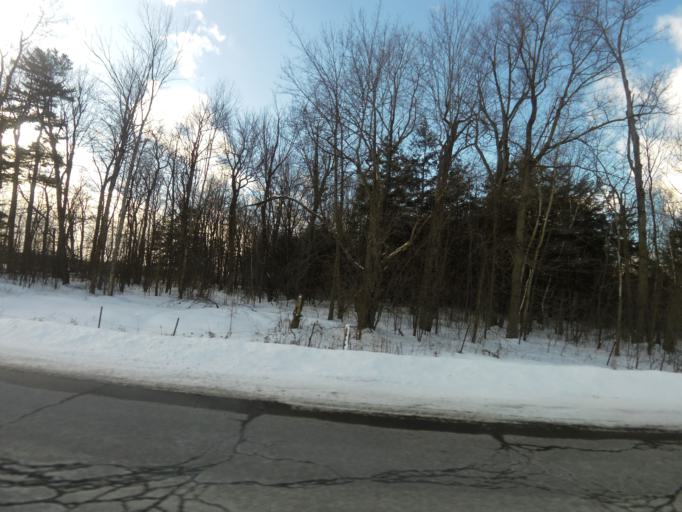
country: CA
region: Ontario
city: Ottawa
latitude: 45.3860
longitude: -75.5766
